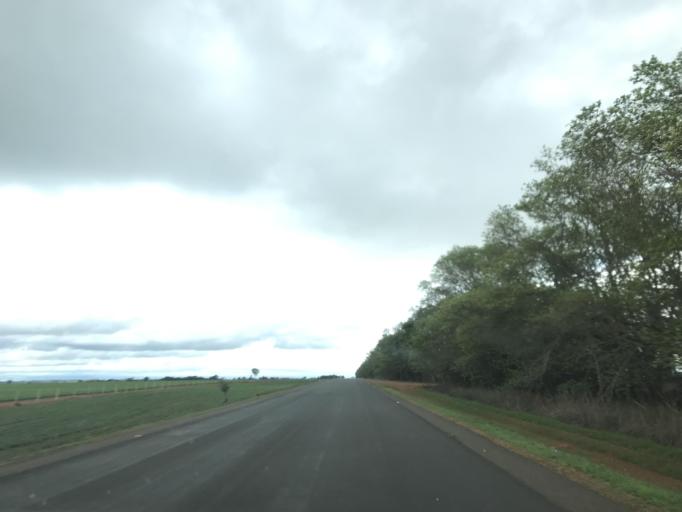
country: BR
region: Goias
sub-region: Vianopolis
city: Vianopolis
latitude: -16.7966
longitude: -48.5203
